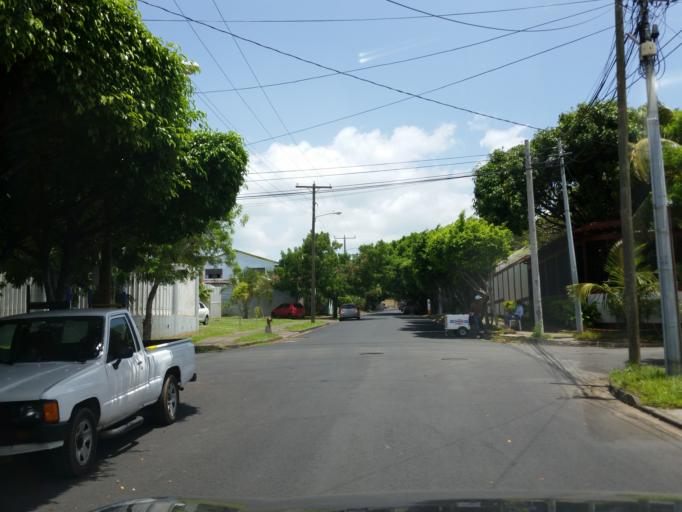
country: NI
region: Managua
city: Managua
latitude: 12.1169
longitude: -86.2689
